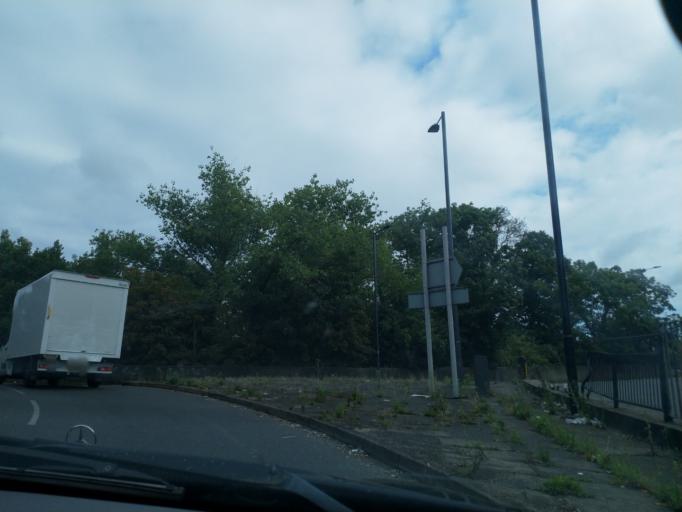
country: GB
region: England
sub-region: Greater London
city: Harrow
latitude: 51.5781
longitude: -0.3260
